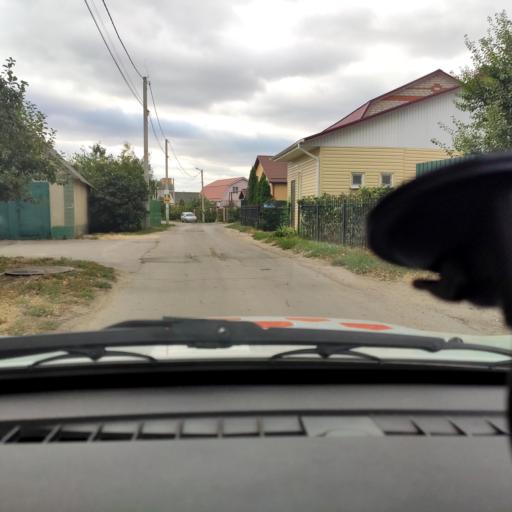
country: RU
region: Voronezj
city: Novaya Usman'
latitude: 51.6278
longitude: 39.3862
